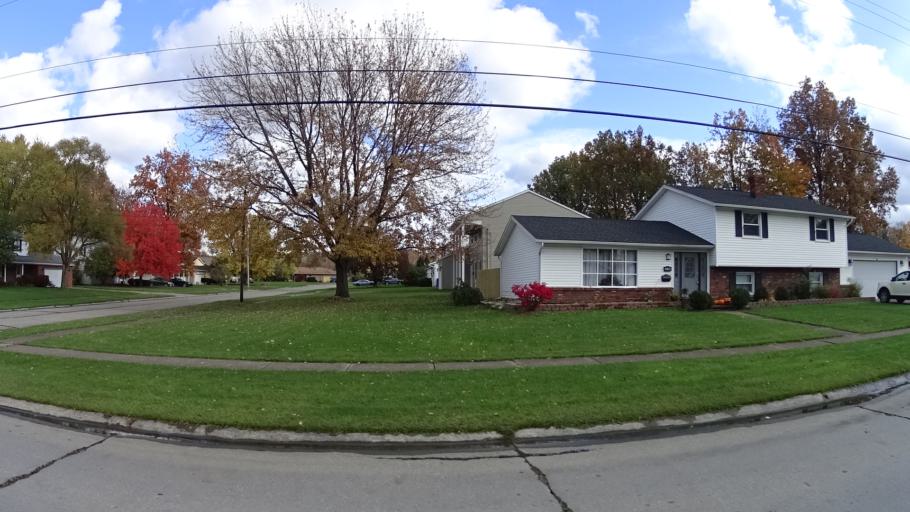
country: US
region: Ohio
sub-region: Lorain County
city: Lorain
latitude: 41.4251
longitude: -82.1899
